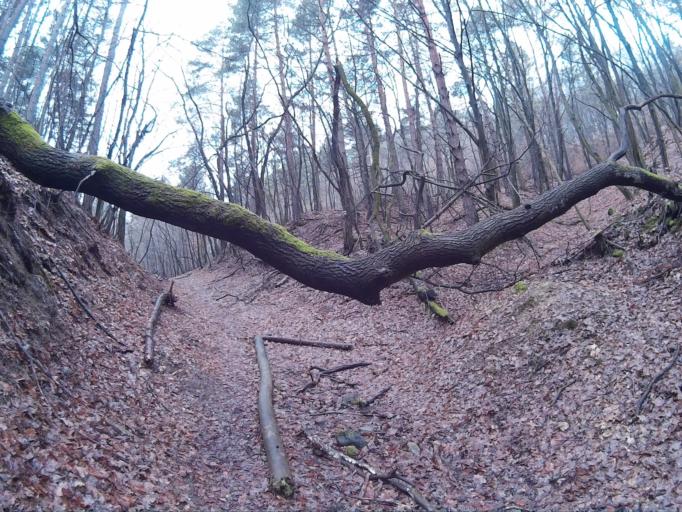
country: HU
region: Borsod-Abauj-Zemplen
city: Sarospatak
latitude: 48.4677
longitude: 21.4710
